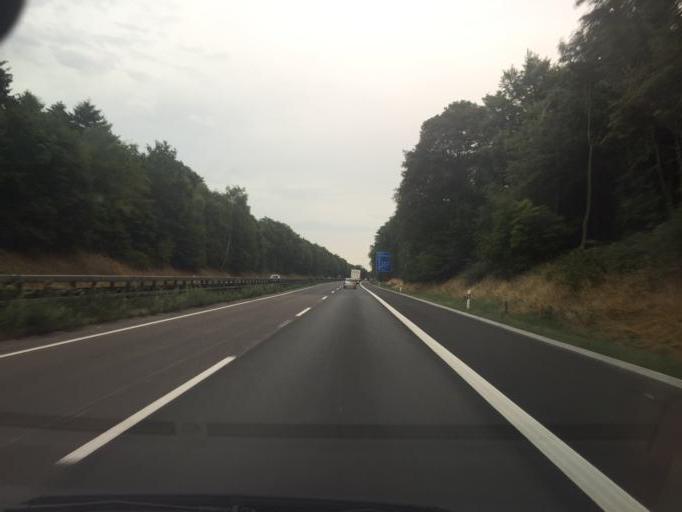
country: DE
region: North Rhine-Westphalia
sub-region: Regierungsbezirk Dusseldorf
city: Viersen
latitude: 51.2201
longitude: 6.3703
